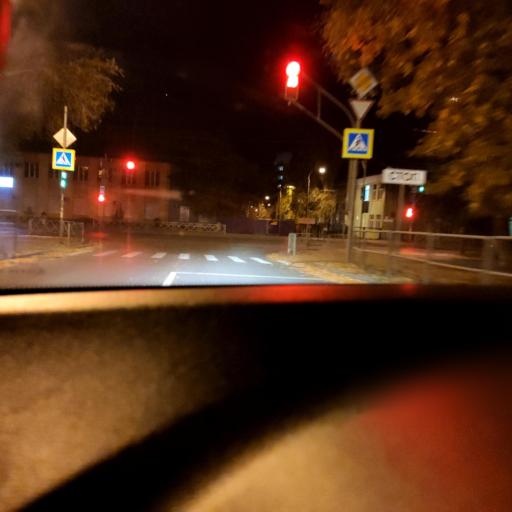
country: RU
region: Samara
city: Samara
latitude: 53.1912
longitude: 50.1303
